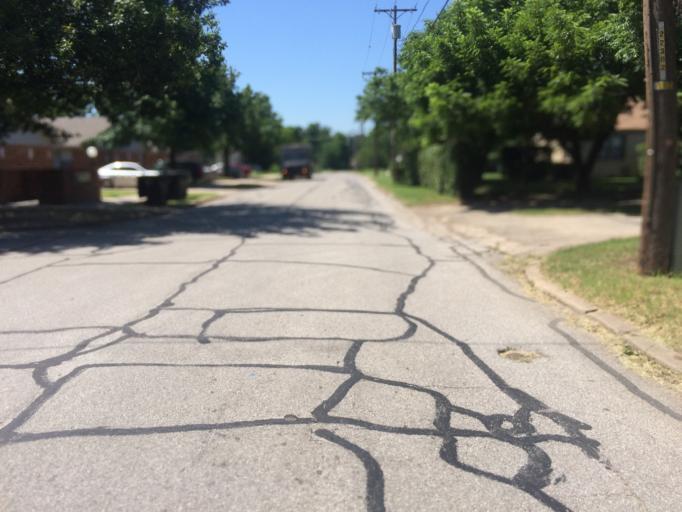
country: US
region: Oklahoma
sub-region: Cleveland County
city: Norman
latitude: 35.2237
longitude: -97.4501
